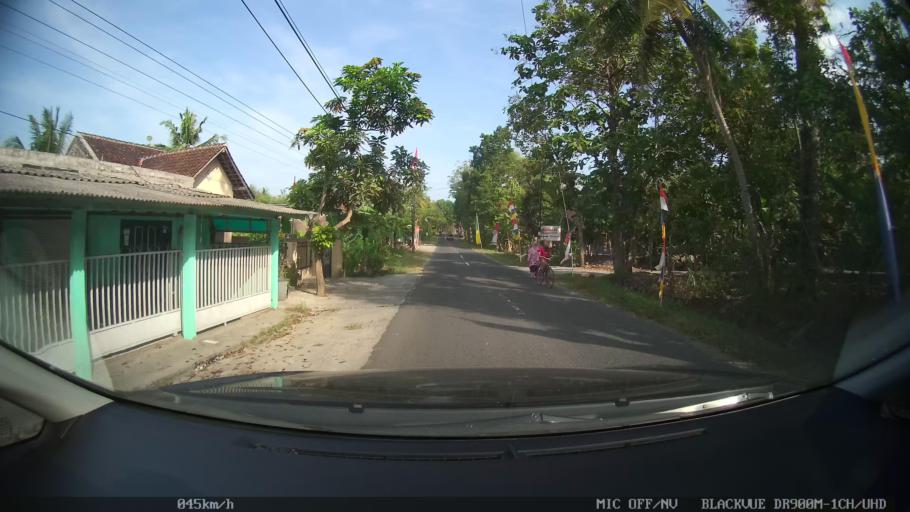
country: ID
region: Daerah Istimewa Yogyakarta
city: Kasihan
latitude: -7.8524
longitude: 110.3184
